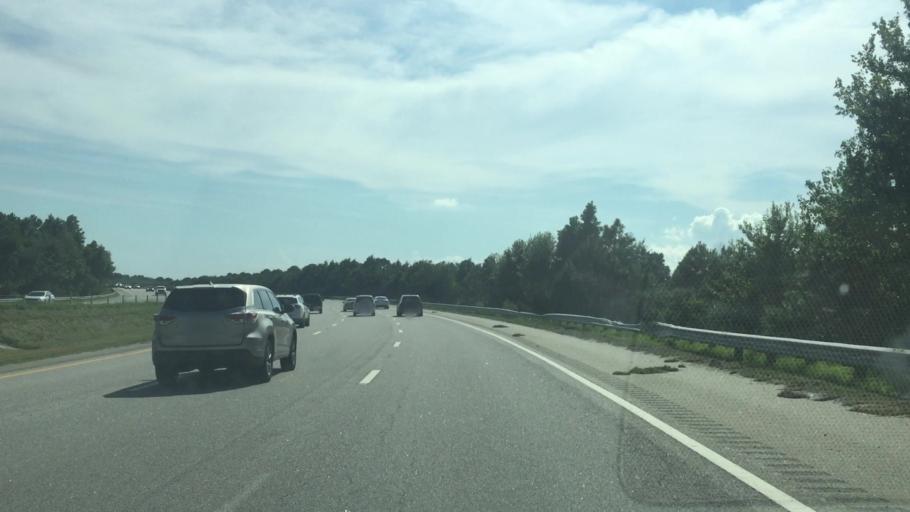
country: US
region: South Carolina
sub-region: Horry County
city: North Myrtle Beach
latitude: 33.8254
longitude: -78.7340
